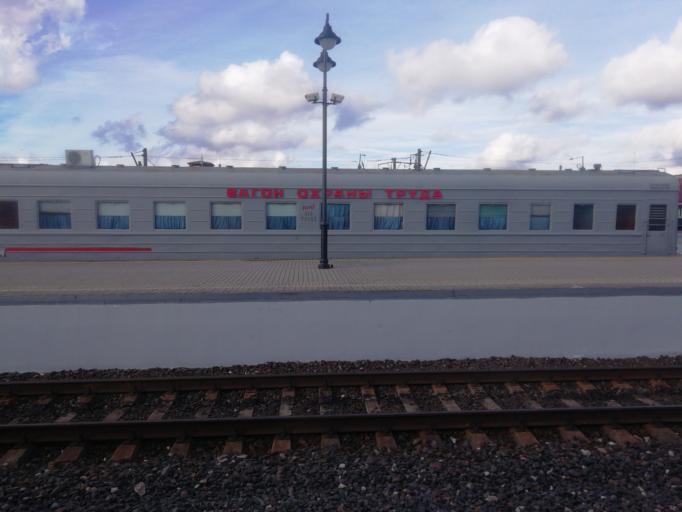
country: RU
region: Kaliningrad
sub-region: Gorod Kaliningrad
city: Kaliningrad
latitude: 54.6942
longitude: 20.4964
